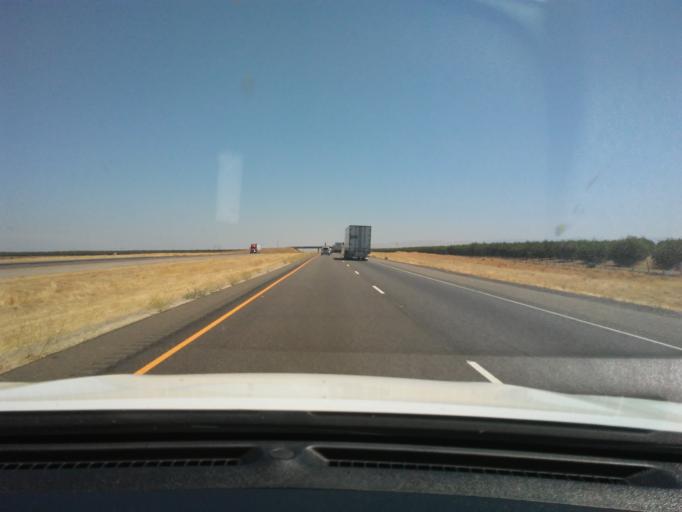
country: US
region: California
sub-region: Merced County
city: South Dos Palos
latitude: 36.7271
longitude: -120.6895
